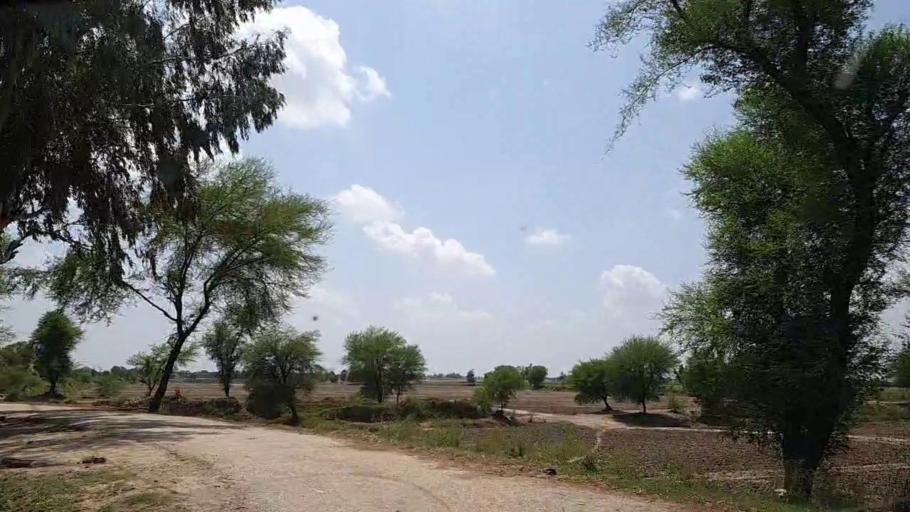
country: PK
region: Sindh
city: Tharu Shah
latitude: 27.0084
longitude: 68.0649
